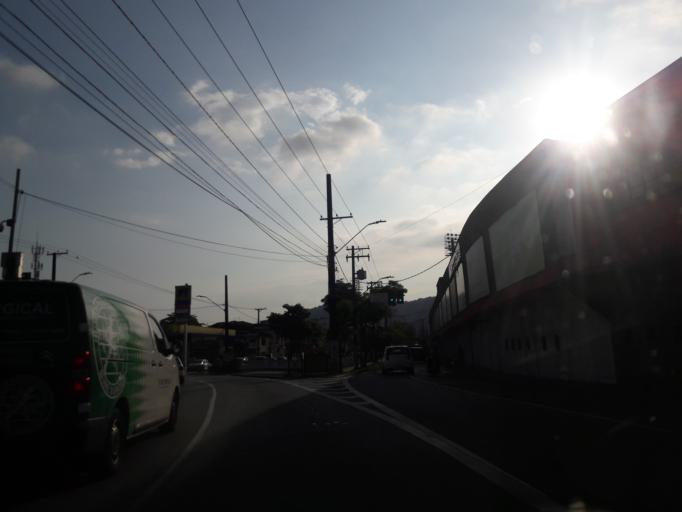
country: BR
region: Sao Paulo
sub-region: Santos
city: Santos
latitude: -23.9472
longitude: -46.3365
